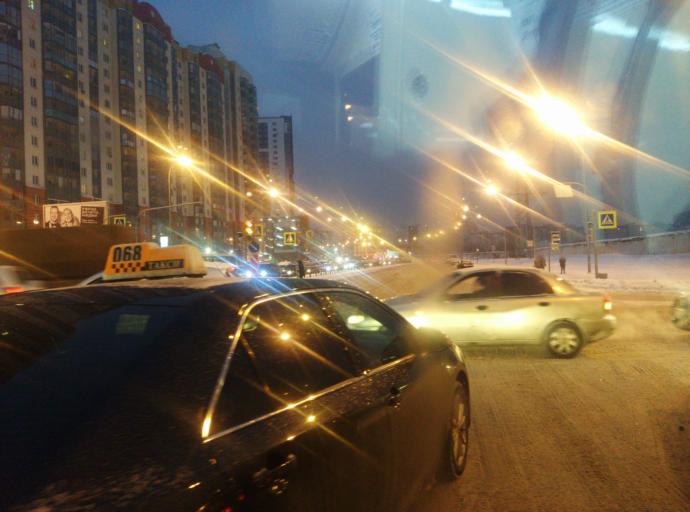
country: RU
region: St.-Petersburg
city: Komendantsky aerodrom
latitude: 60.0211
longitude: 30.2640
